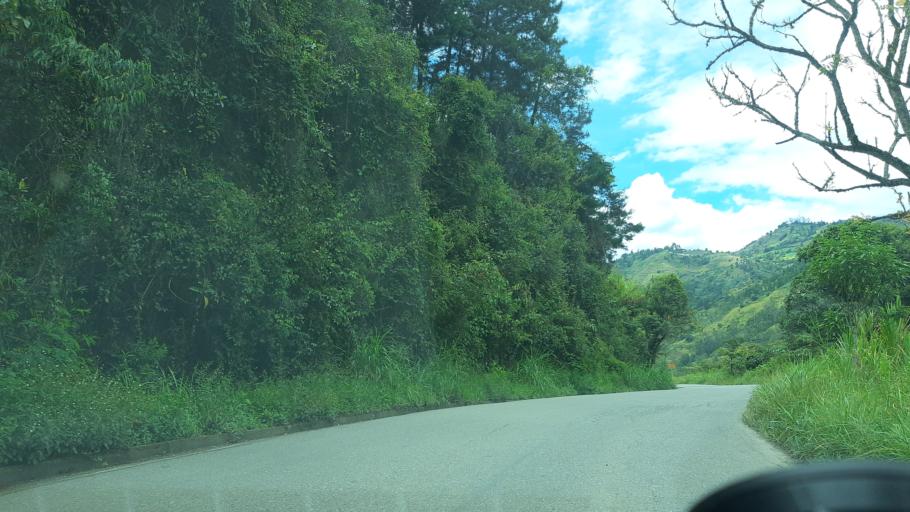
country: CO
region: Boyaca
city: Garagoa
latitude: 5.0447
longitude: -73.3876
